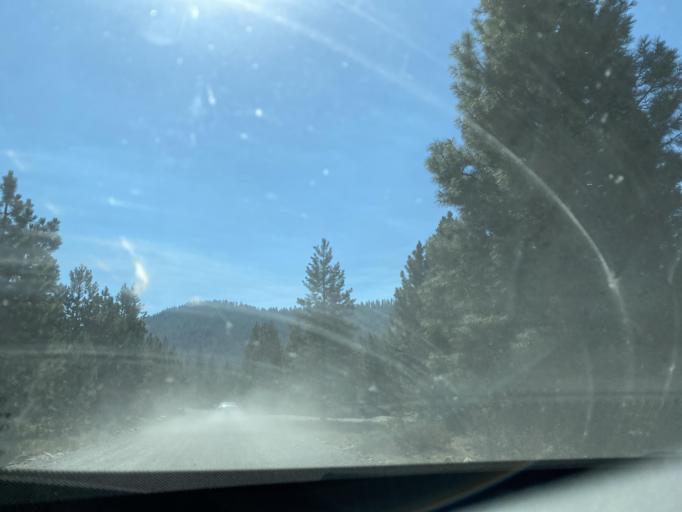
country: US
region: Oregon
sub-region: Deschutes County
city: Deschutes River Woods
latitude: 44.0345
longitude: -121.5263
